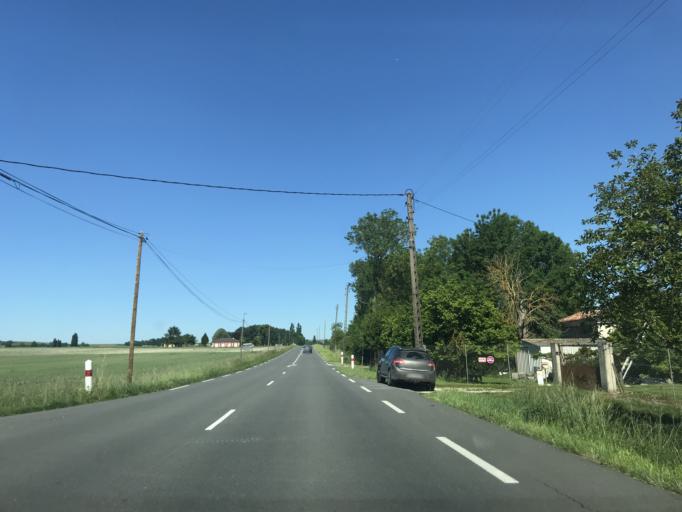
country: FR
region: Poitou-Charentes
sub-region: Departement de la Charente
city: Barbezieux-Saint-Hilaire
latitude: 45.4963
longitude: -0.2296
